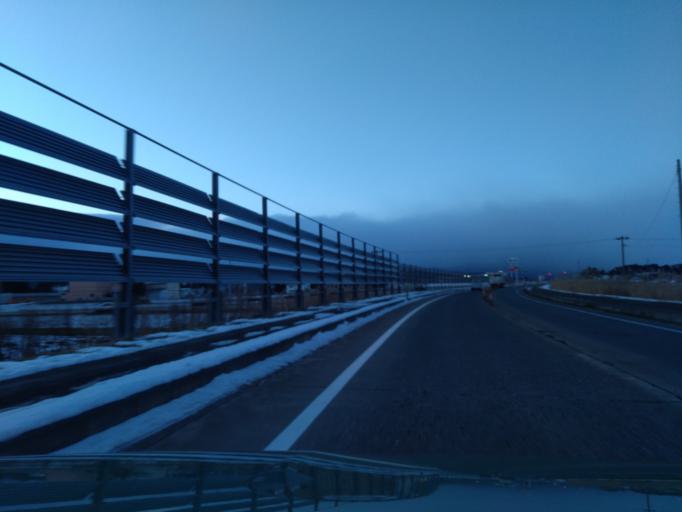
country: JP
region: Iwate
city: Shizukuishi
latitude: 39.6934
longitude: 140.9812
